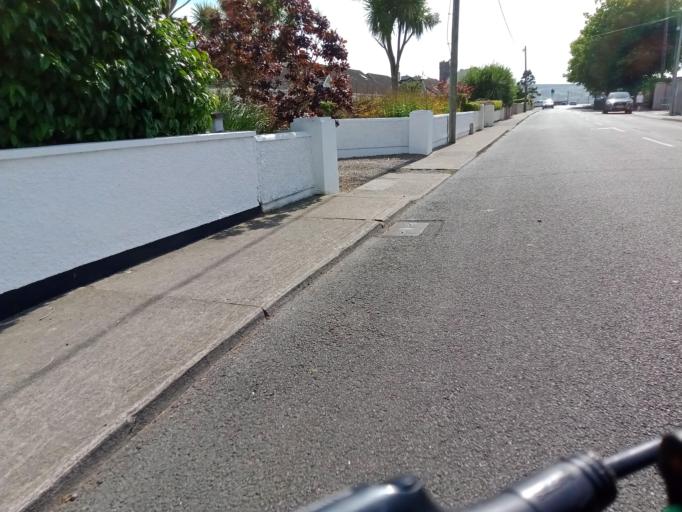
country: IE
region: Munster
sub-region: Waterford
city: Dungarvan
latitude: 52.0896
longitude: -7.6096
